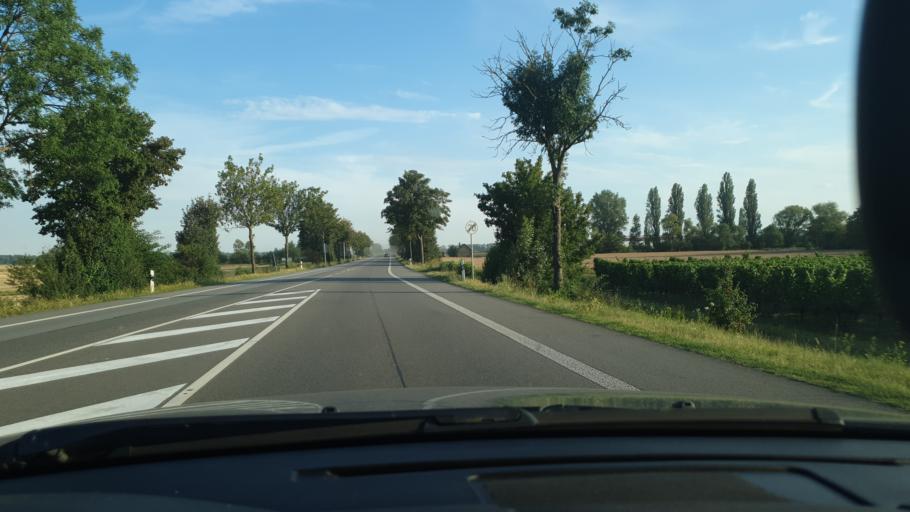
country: DE
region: Rheinland-Pfalz
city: Mettenheim
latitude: 49.7348
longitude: 8.3504
